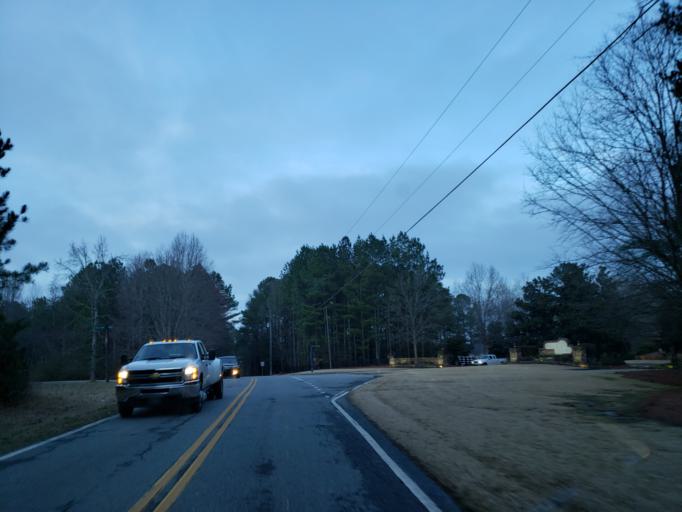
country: US
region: Georgia
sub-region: Cherokee County
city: Ball Ground
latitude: 34.2401
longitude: -84.3357
